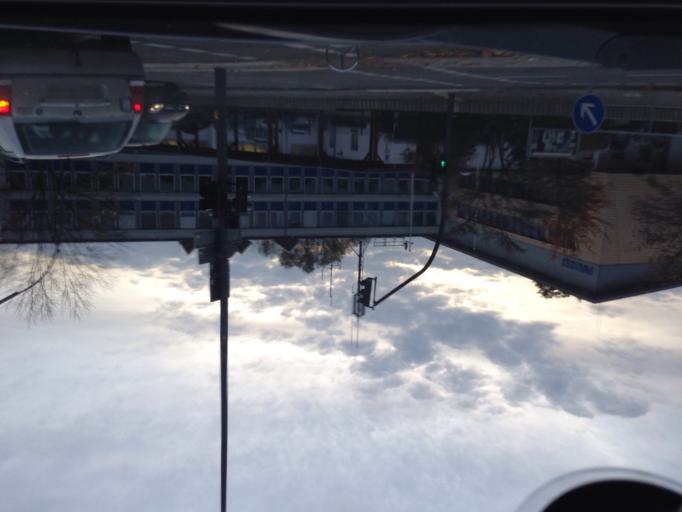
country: DE
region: Hamburg
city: Farmsen-Berne
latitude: 53.6002
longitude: 10.1520
